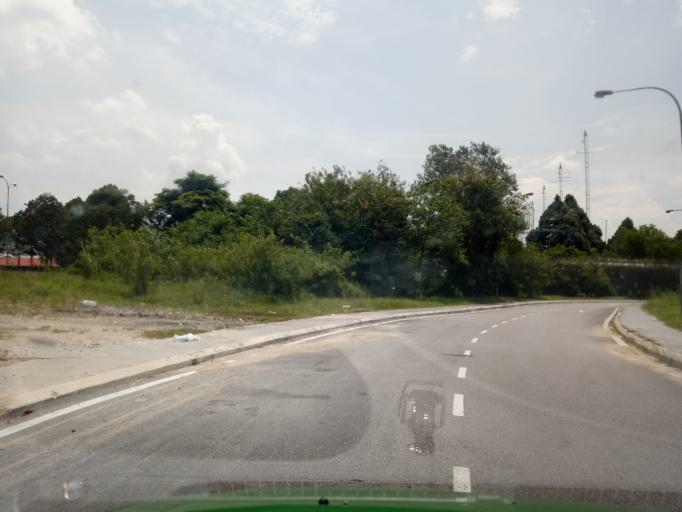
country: MY
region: Selangor
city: Kampong Baharu Balakong
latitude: 3.0029
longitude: 101.7842
